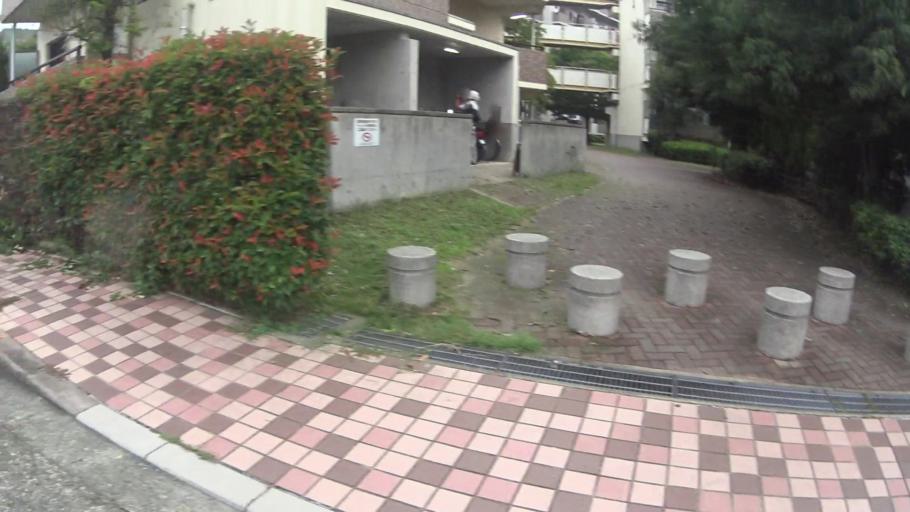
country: JP
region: Kyoto
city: Muko
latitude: 34.9263
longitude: 135.7034
